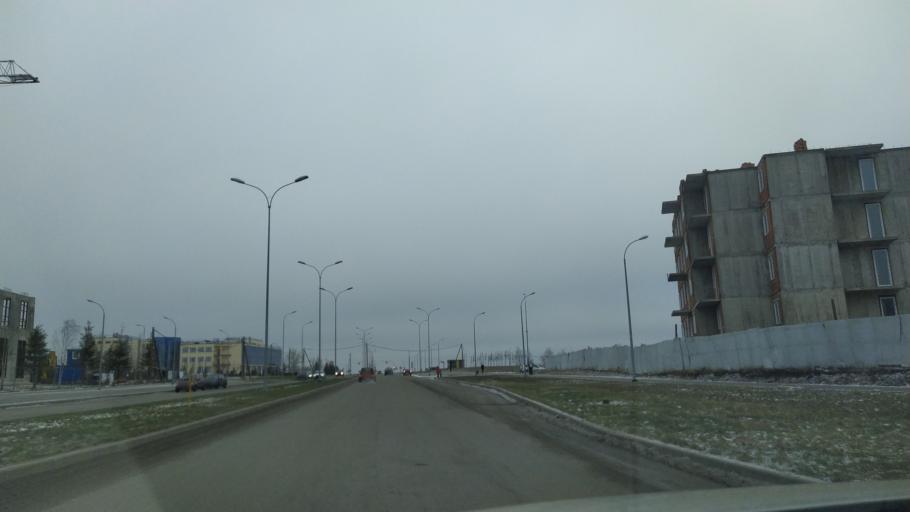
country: RU
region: St.-Petersburg
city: Aleksandrovskaya
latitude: 59.7569
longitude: 30.3676
